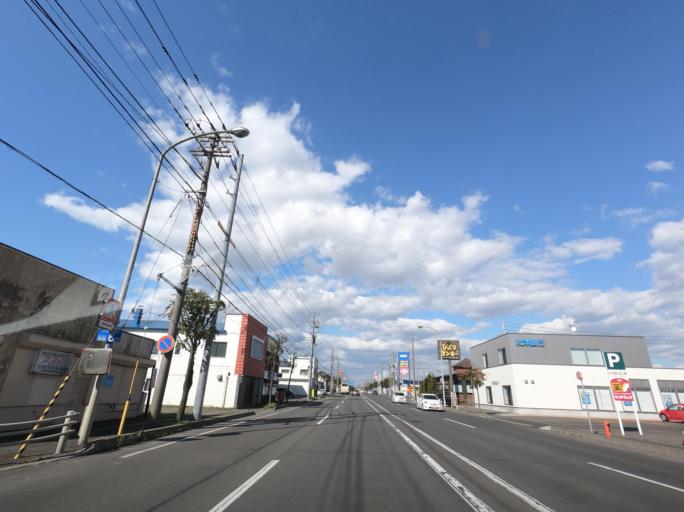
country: JP
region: Hokkaido
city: Kushiro
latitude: 43.0102
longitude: 144.3602
